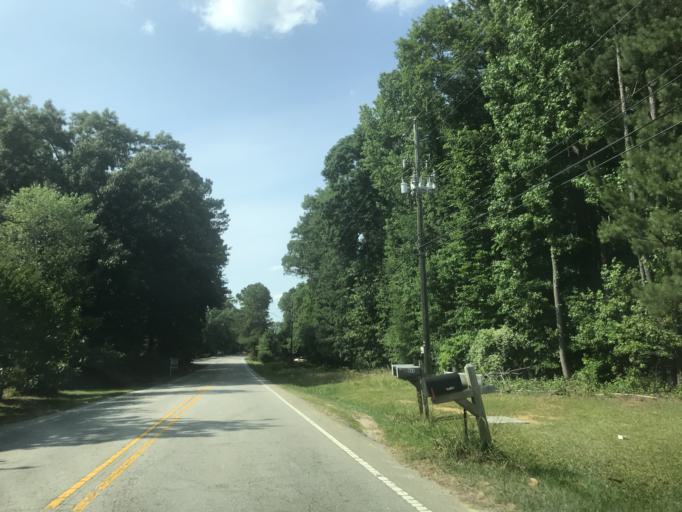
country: US
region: North Carolina
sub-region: Wake County
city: Cary
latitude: 35.7927
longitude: -78.7348
